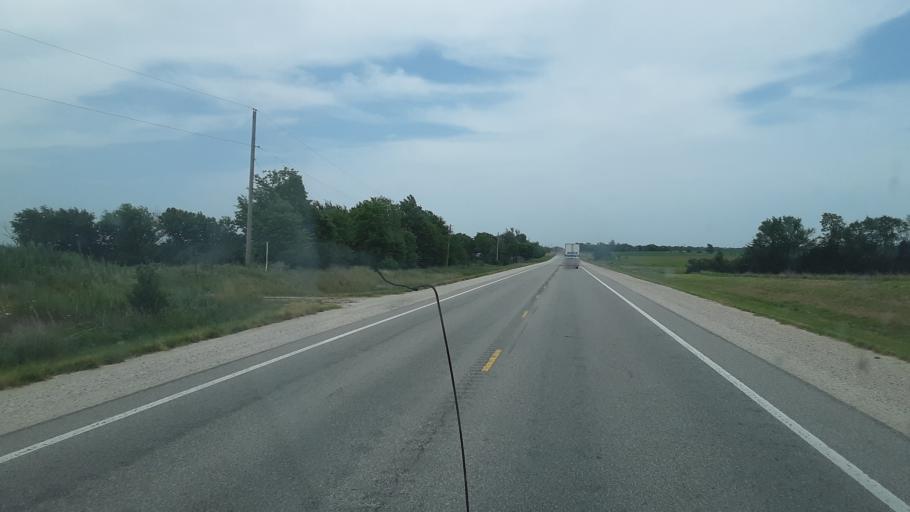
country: US
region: Kansas
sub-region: Allen County
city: Iola
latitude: 37.9217
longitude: -95.2178
